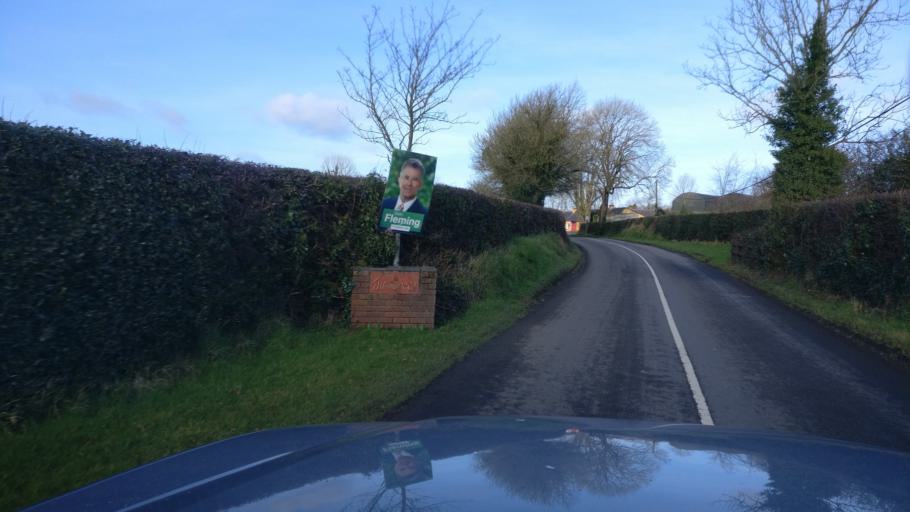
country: IE
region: Leinster
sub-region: Kilkenny
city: Castlecomer
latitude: 52.8875
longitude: -7.1610
